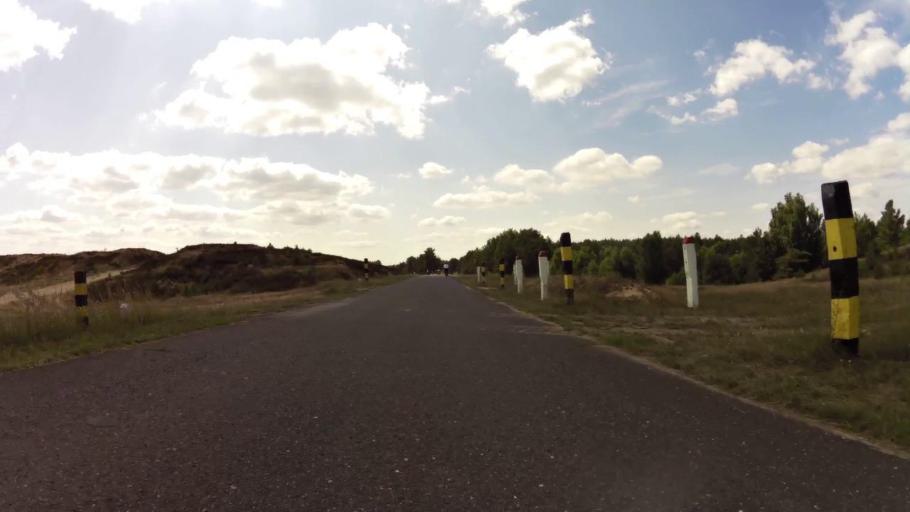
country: PL
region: West Pomeranian Voivodeship
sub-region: Powiat drawski
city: Drawsko Pomorskie
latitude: 53.4125
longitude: 15.7378
